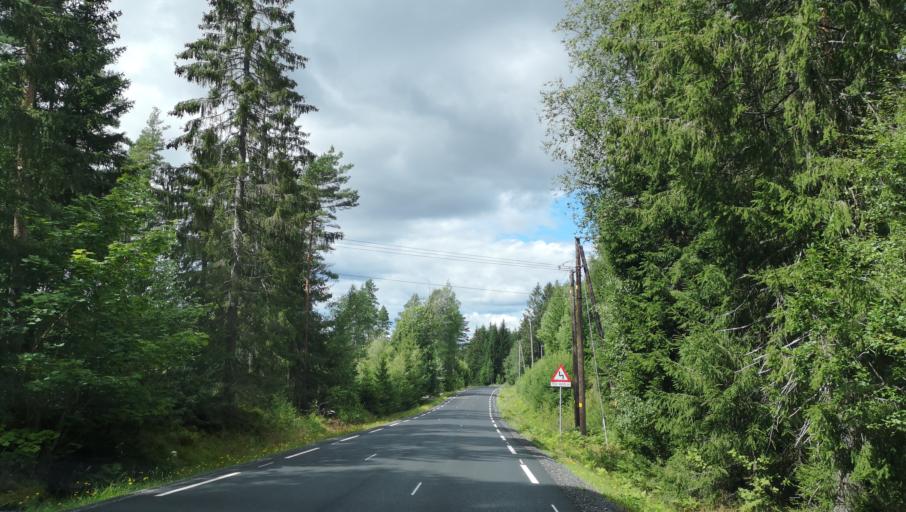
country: NO
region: Ostfold
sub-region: Hobol
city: Tomter
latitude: 59.6800
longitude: 10.9479
